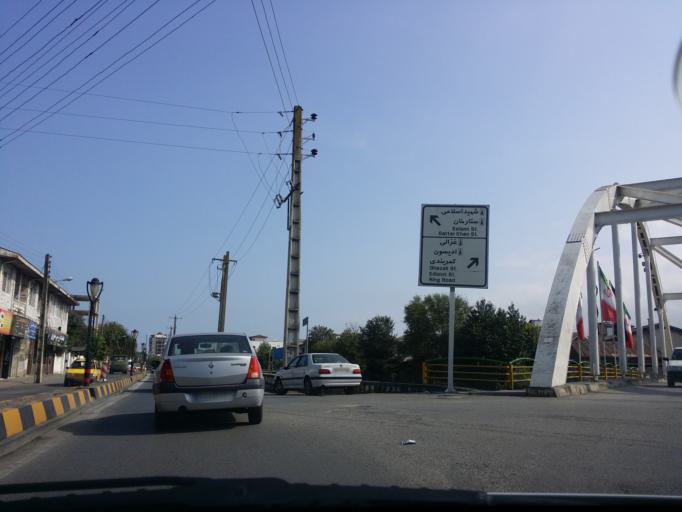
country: IR
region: Mazandaran
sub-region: Nowshahr
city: Nowshahr
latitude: 36.6451
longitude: 51.4998
